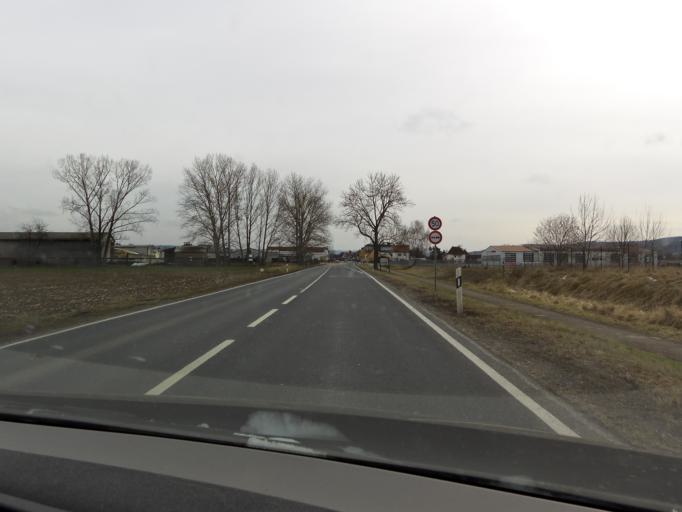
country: DE
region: Thuringia
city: Breitungen
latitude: 50.7695
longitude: 10.3189
